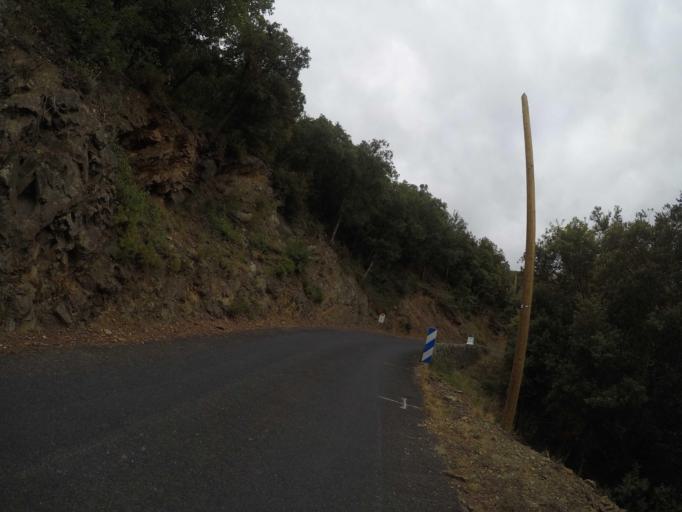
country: FR
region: Languedoc-Roussillon
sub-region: Departement des Pyrenees-Orientales
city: Ille-sur-Tet
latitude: 42.6415
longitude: 2.6223
